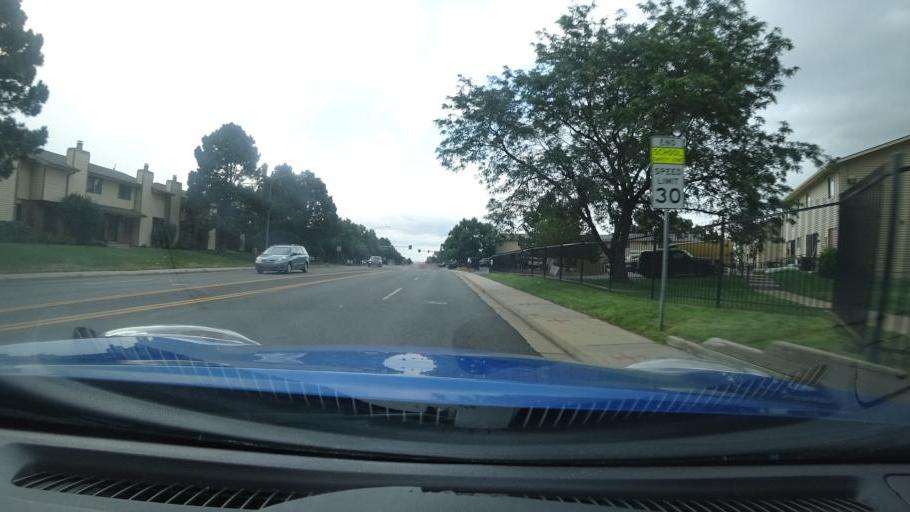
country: US
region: Colorado
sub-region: Adams County
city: Aurora
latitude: 39.6954
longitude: -104.8192
